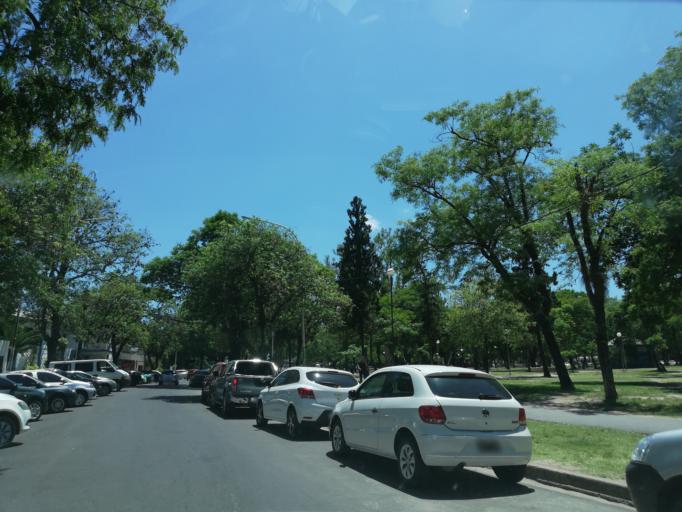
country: AR
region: Corrientes
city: Corrientes
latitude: -27.4595
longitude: -58.8300
